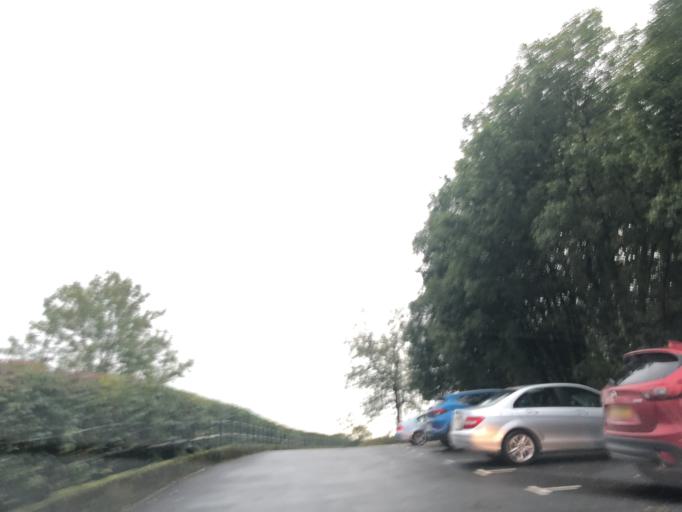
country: GB
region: England
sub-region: Cumbria
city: Windermere
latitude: 54.4257
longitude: -2.9048
